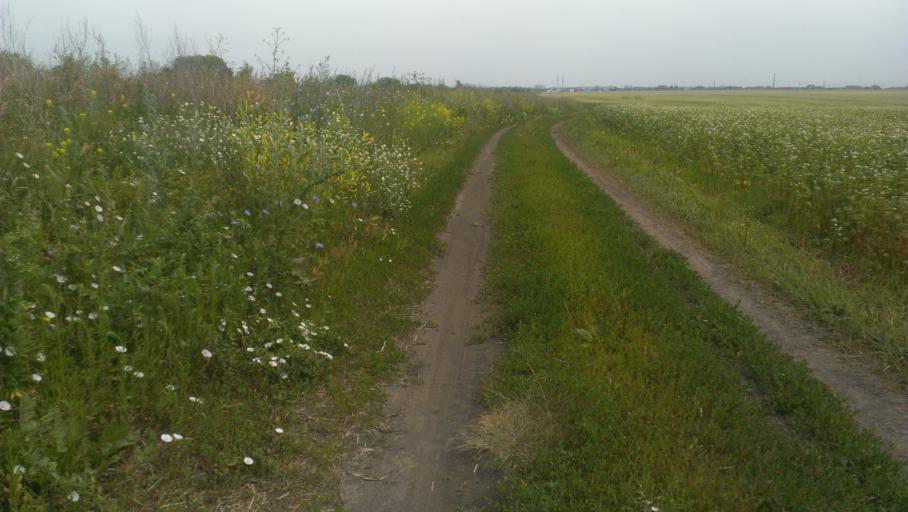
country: RU
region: Altai Krai
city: Novosilikatnyy
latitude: 53.3789
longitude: 83.6351
